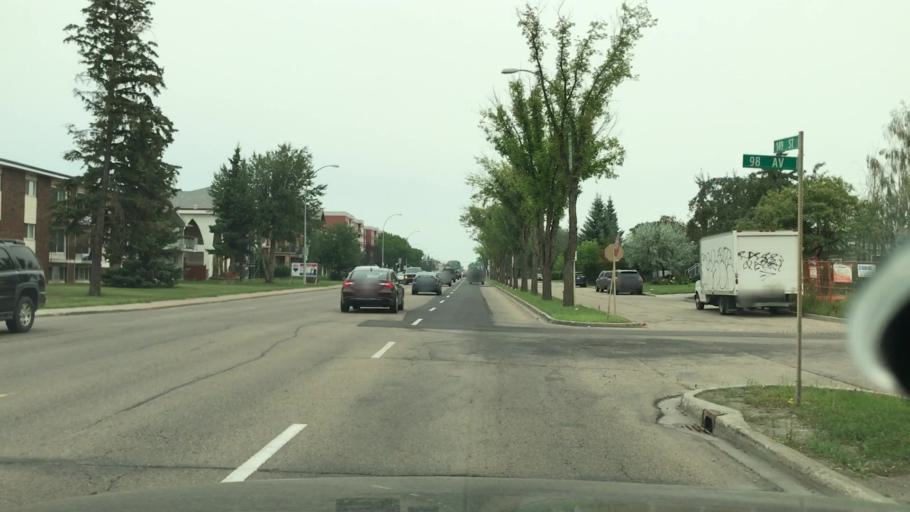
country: CA
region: Alberta
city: Edmonton
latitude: 53.5360
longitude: -113.5779
